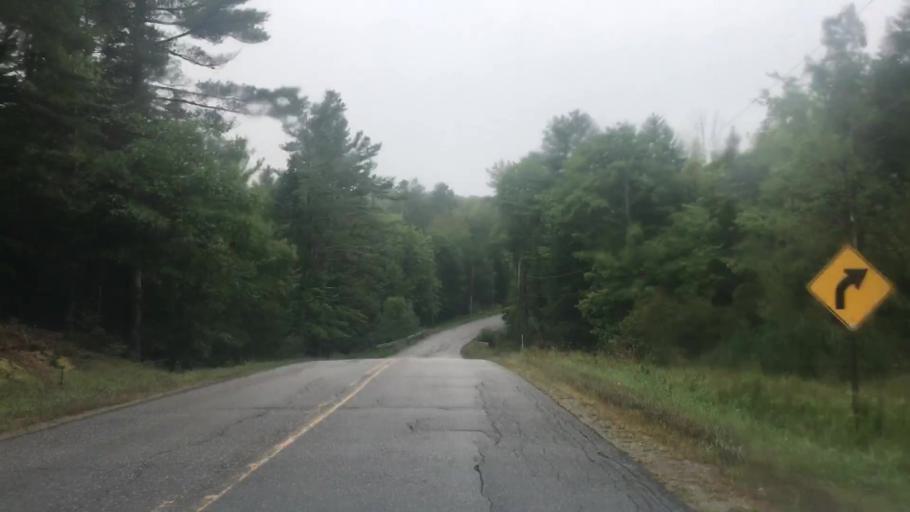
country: US
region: Maine
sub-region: Waldo County
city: Stockton Springs
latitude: 44.5408
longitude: -68.9052
